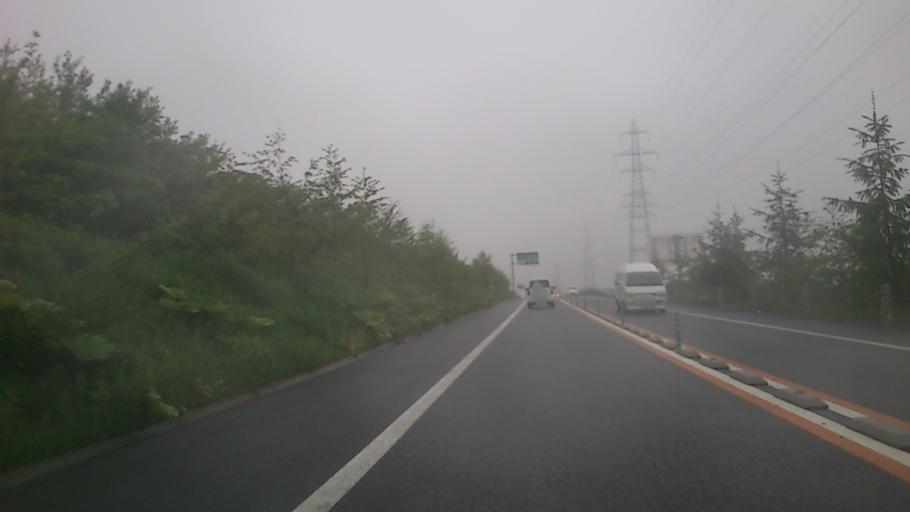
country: JP
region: Hokkaido
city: Kushiro
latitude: 43.0234
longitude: 144.4156
